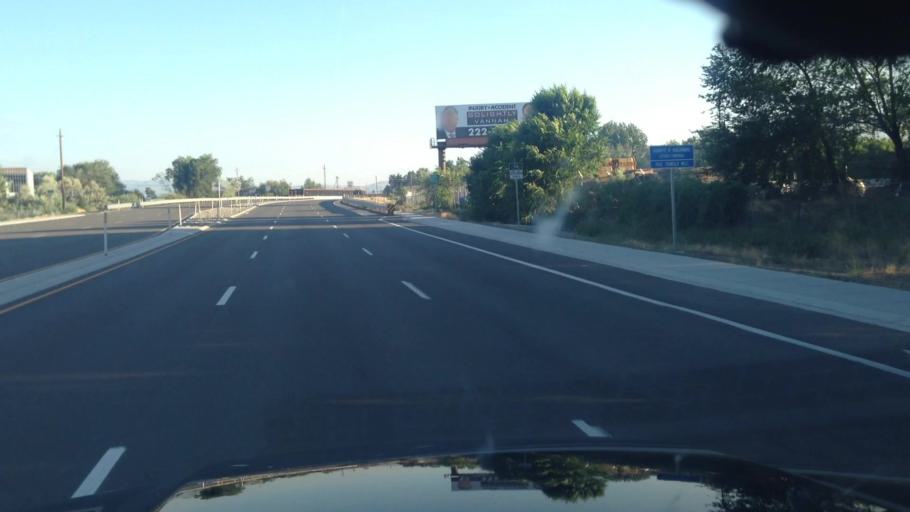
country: US
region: Nevada
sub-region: Washoe County
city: Sparks
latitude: 39.5202
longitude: -119.7404
